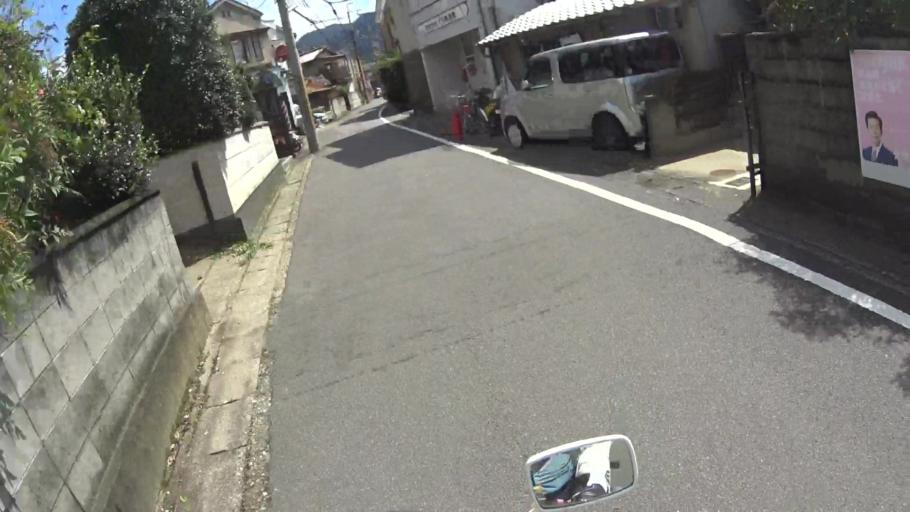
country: JP
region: Shiga Prefecture
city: Otsu-shi
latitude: 34.9714
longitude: 135.8053
